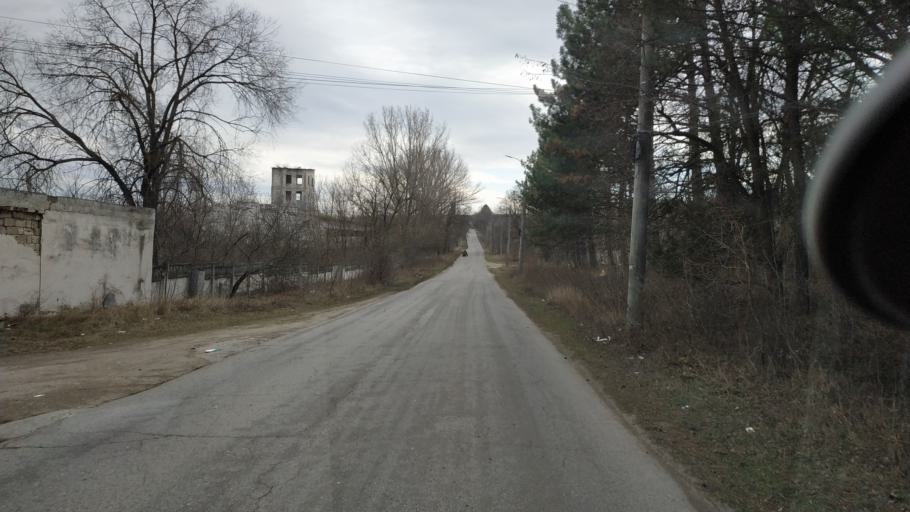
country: MD
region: Chisinau
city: Vadul lui Voda
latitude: 47.1021
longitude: 29.0670
